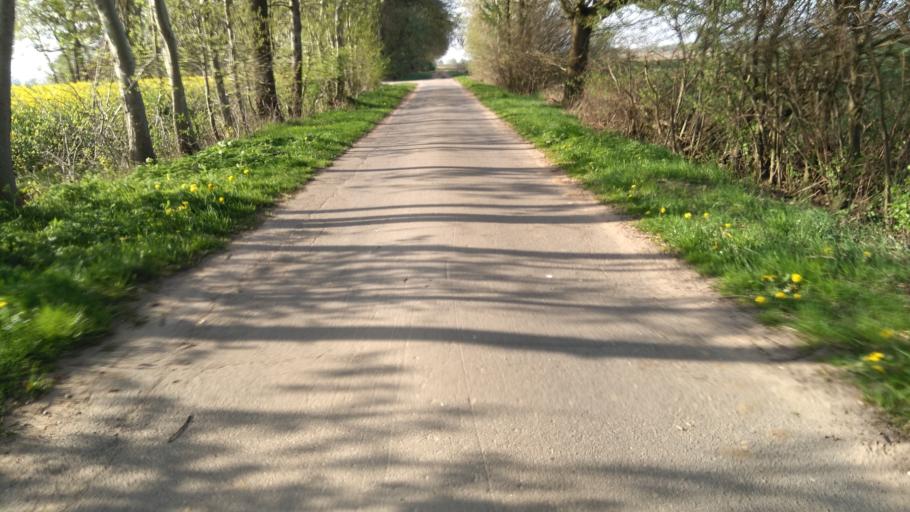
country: DE
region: Lower Saxony
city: Apensen
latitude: 53.4326
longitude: 9.6485
